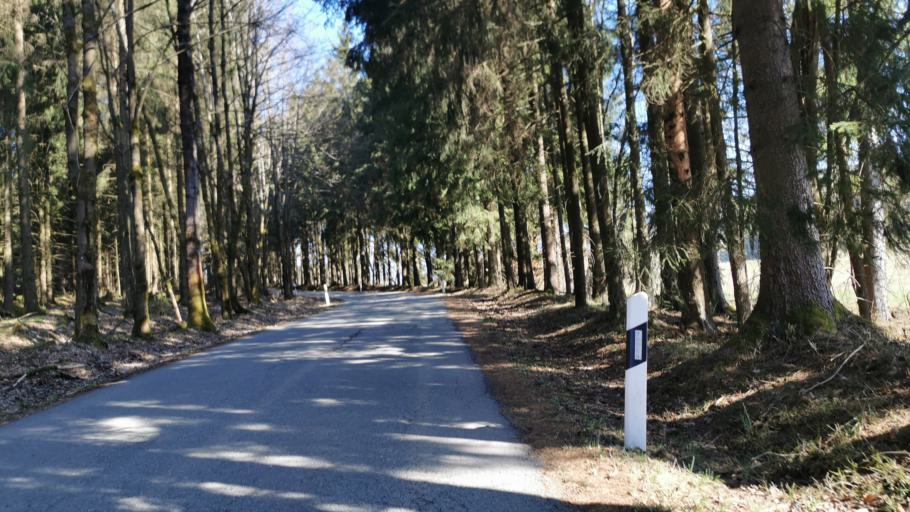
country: DE
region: Bavaria
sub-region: Upper Franconia
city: Reichenbach
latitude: 50.4440
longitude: 11.4050
